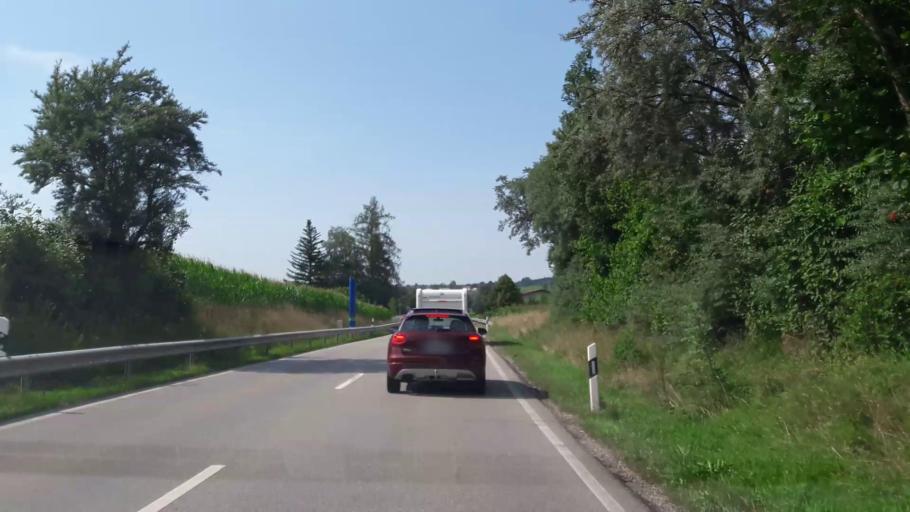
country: DE
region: Bavaria
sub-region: Upper Bavaria
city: Teisendorf
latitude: 47.8449
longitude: 12.8138
